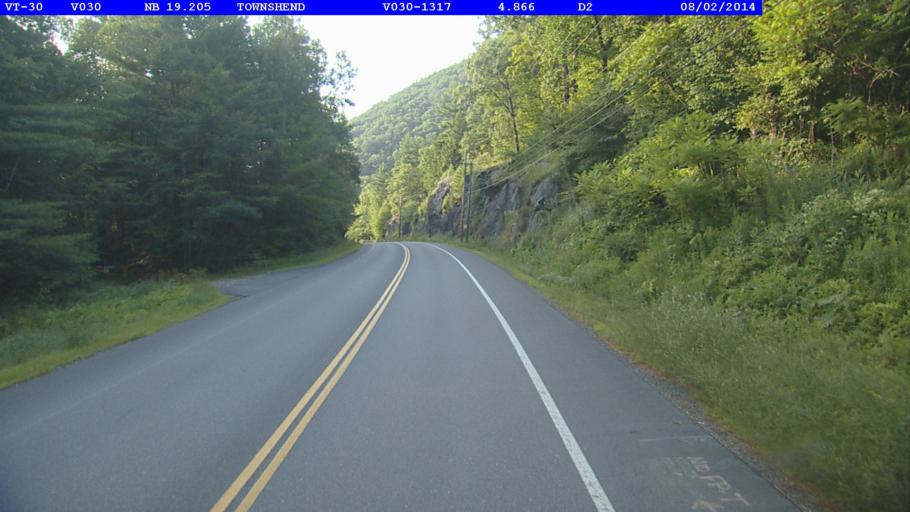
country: US
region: Vermont
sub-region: Windham County
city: Newfane
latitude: 43.0645
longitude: -72.6979
